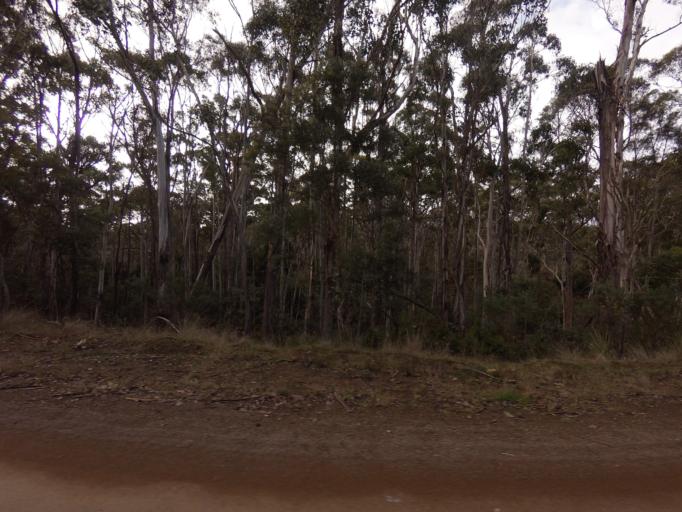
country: AU
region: Tasmania
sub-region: Derwent Valley
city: New Norfolk
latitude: -42.7528
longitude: 146.8756
